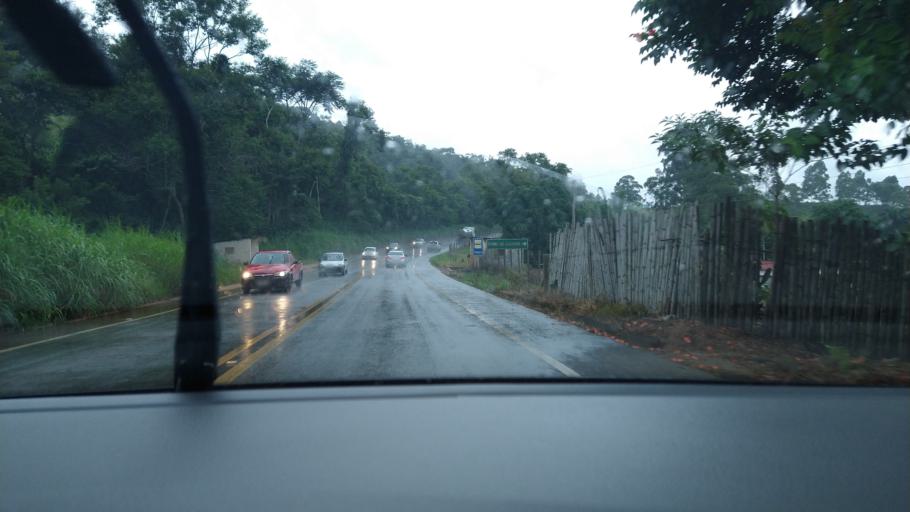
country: BR
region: Minas Gerais
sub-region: Vicosa
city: Vicosa
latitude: -20.6148
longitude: -42.8681
